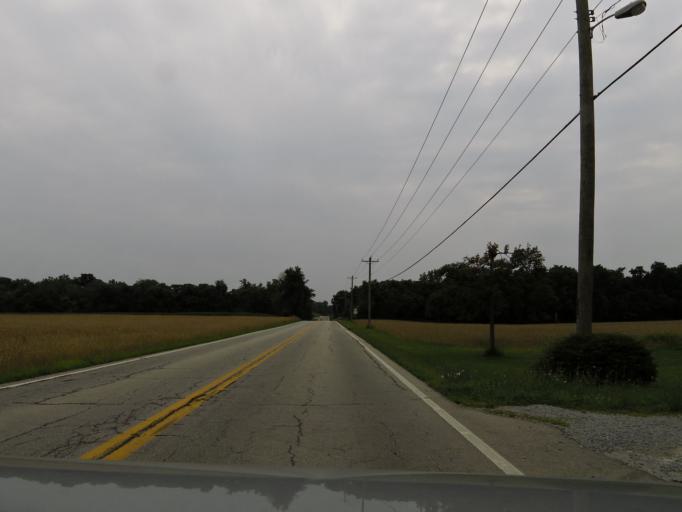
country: US
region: Ohio
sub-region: Clinton County
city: Blanchester
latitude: 39.2601
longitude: -83.9031
